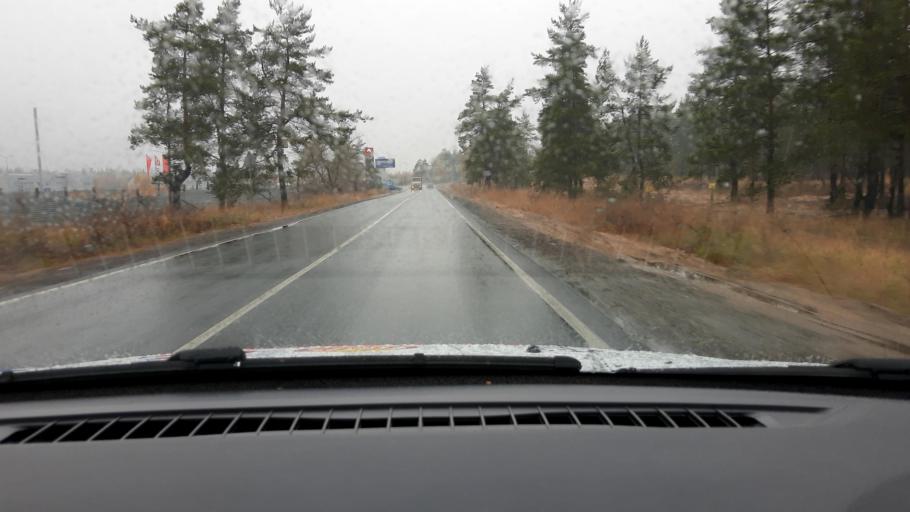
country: RU
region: Nizjnij Novgorod
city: Babino
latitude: 56.2988
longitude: 43.5962
